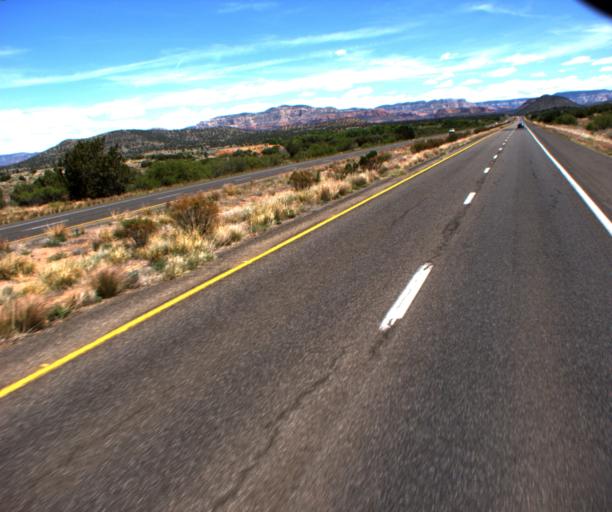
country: US
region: Arizona
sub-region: Yavapai County
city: Cornville
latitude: 34.8190
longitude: -111.9012
